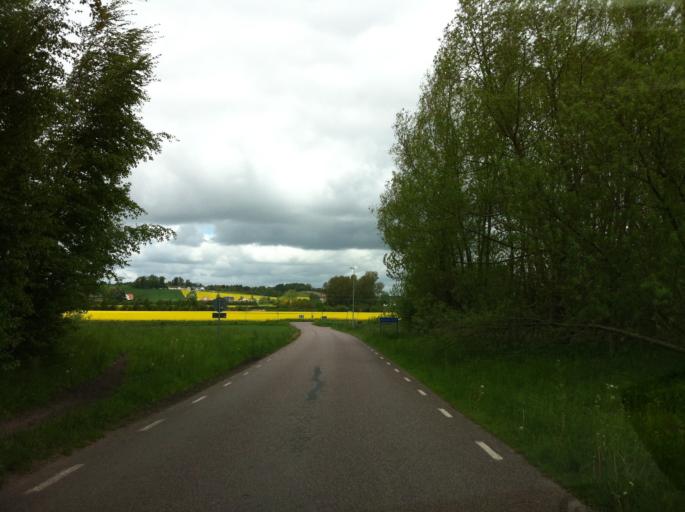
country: SE
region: Skane
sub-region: Kavlinge Kommun
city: Kaevlinge
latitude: 55.8119
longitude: 13.0585
